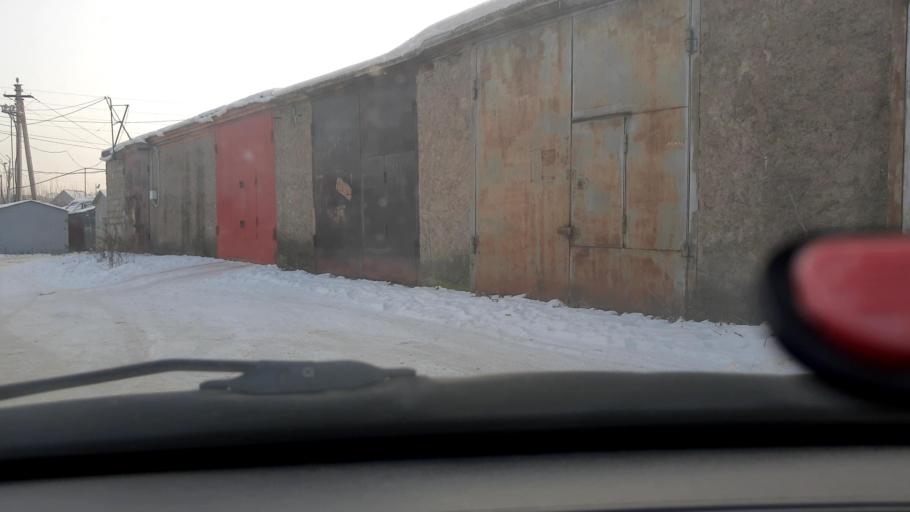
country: RU
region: Bashkortostan
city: Ufa
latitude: 54.8097
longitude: 56.1490
